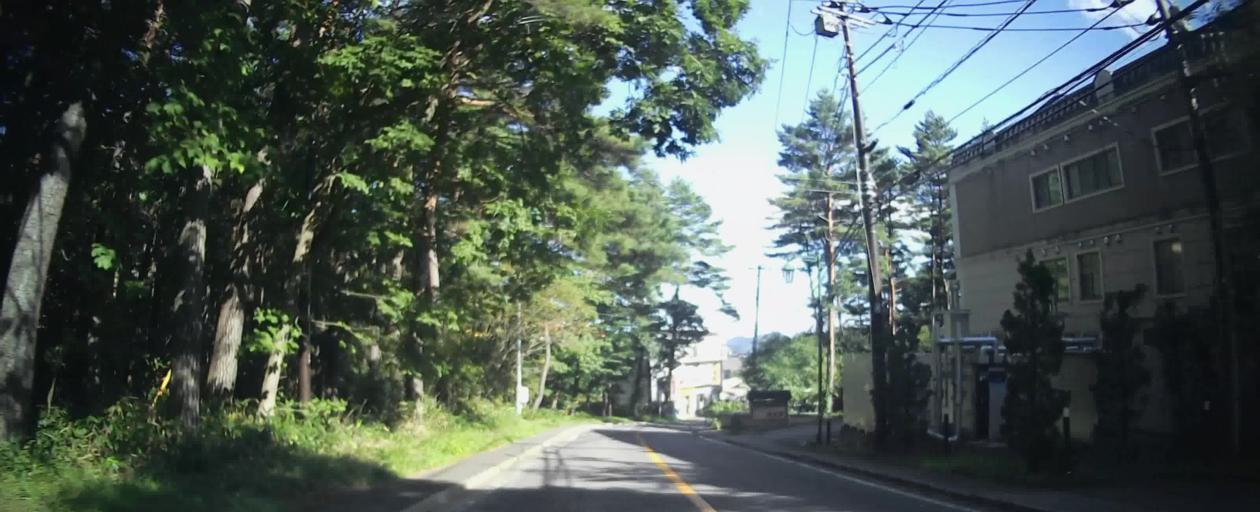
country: JP
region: Gunma
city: Nakanojomachi
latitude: 36.6273
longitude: 138.5926
